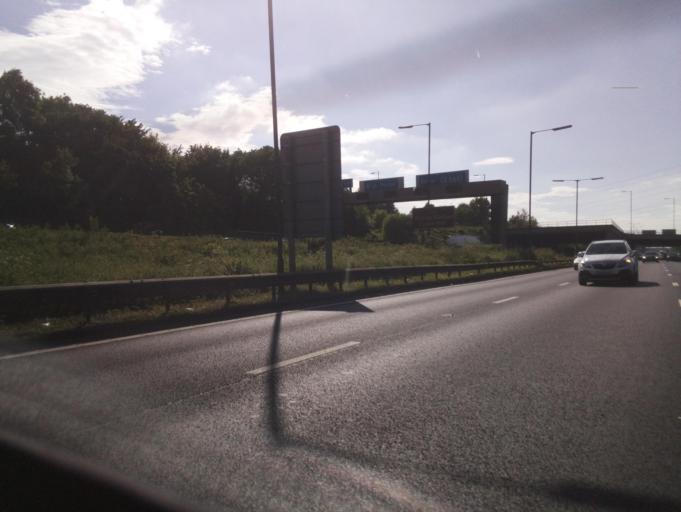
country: GB
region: England
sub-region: Borough of Bolton
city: Kearsley
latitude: 53.5285
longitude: -2.3655
